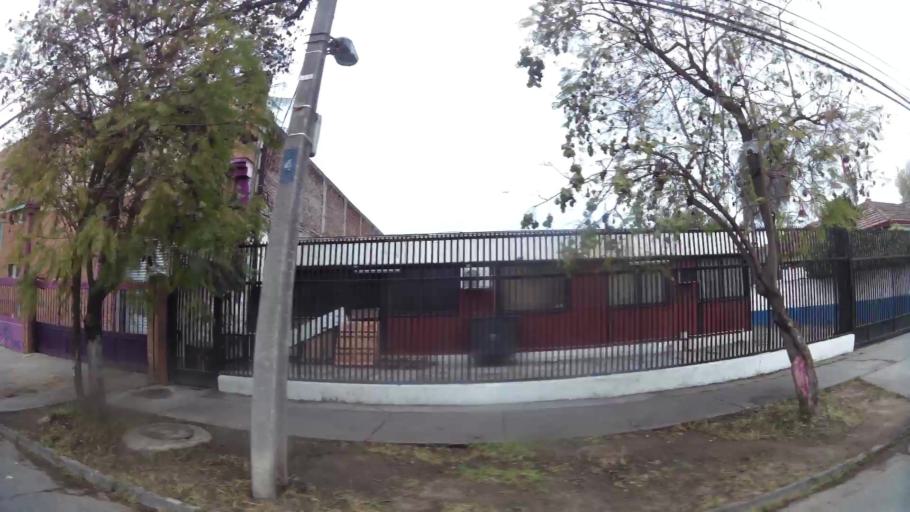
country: CL
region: Santiago Metropolitan
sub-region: Provincia de Santiago
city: Villa Presidente Frei, Nunoa, Santiago, Chile
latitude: -33.4718
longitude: -70.6118
